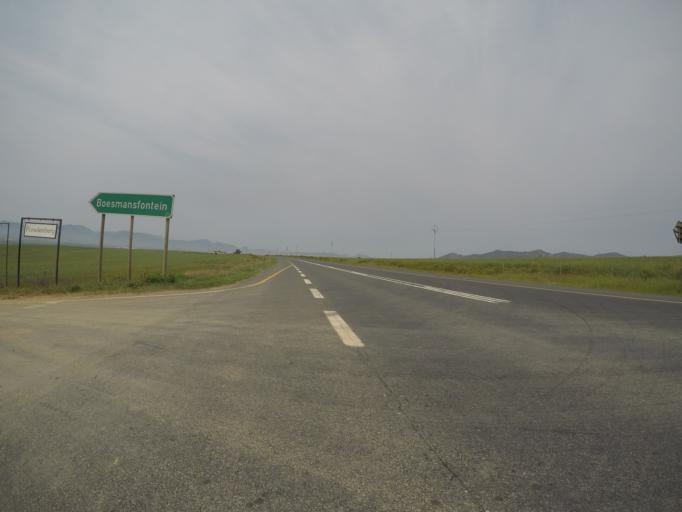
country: ZA
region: Western Cape
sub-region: West Coast District Municipality
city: Malmesbury
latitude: -33.5273
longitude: 18.8481
